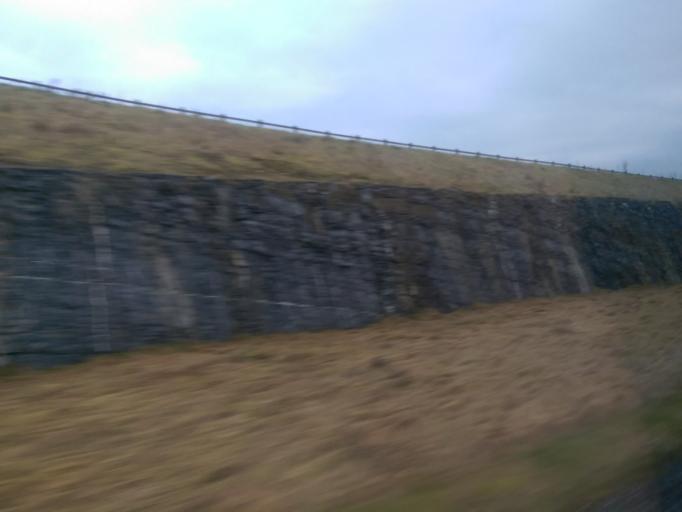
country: IE
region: Connaught
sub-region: County Galway
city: Loughrea
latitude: 53.2815
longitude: -8.4334
